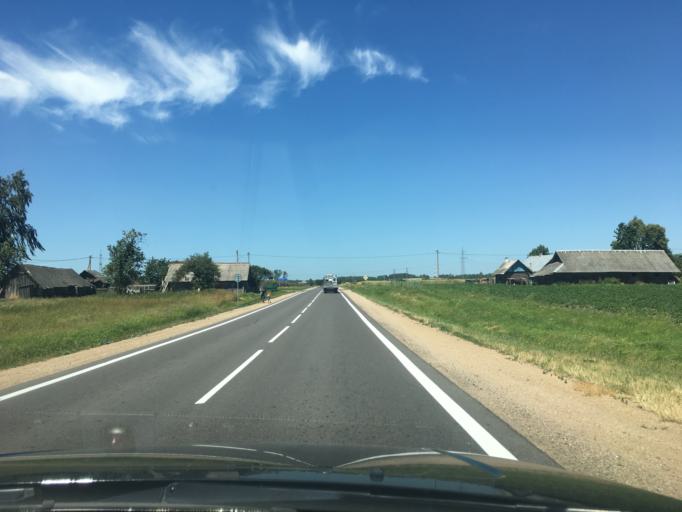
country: BY
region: Grodnenskaya
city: Hal'shany
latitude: 54.1003
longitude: 25.9148
